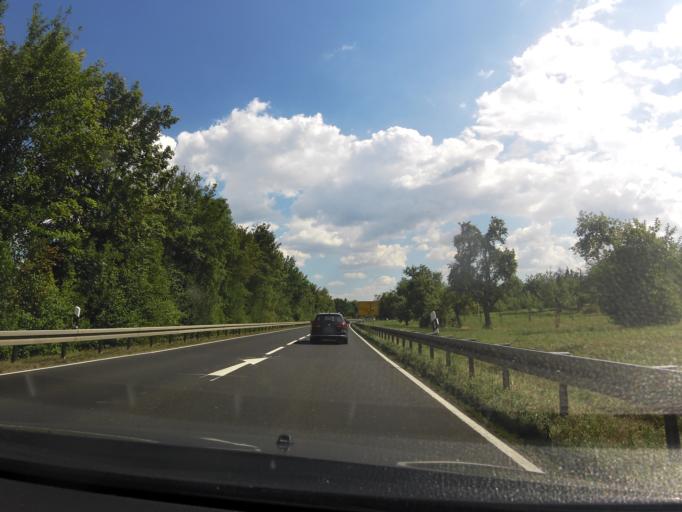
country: DE
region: Bavaria
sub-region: Regierungsbezirk Unterfranken
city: Margetshochheim
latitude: 49.8458
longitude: 9.8583
